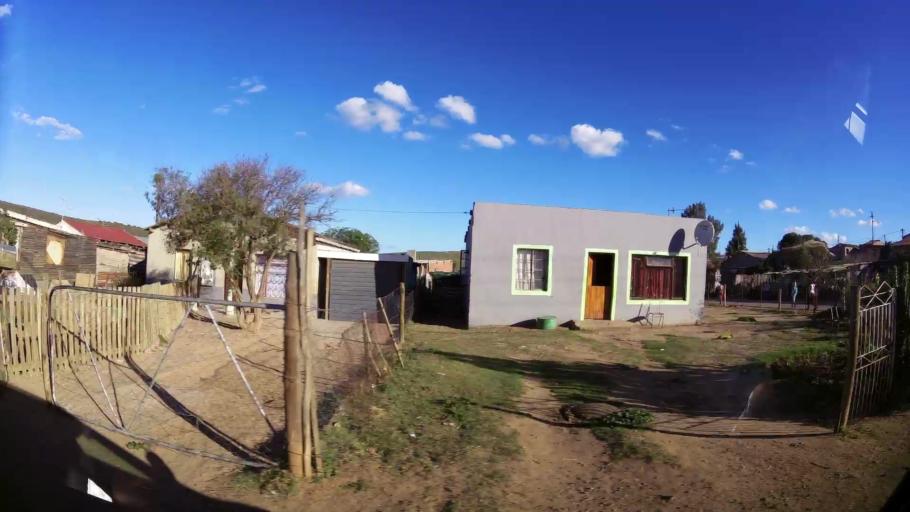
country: ZA
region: Western Cape
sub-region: Eden District Municipality
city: Riversdale
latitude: -34.1063
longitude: 20.9678
